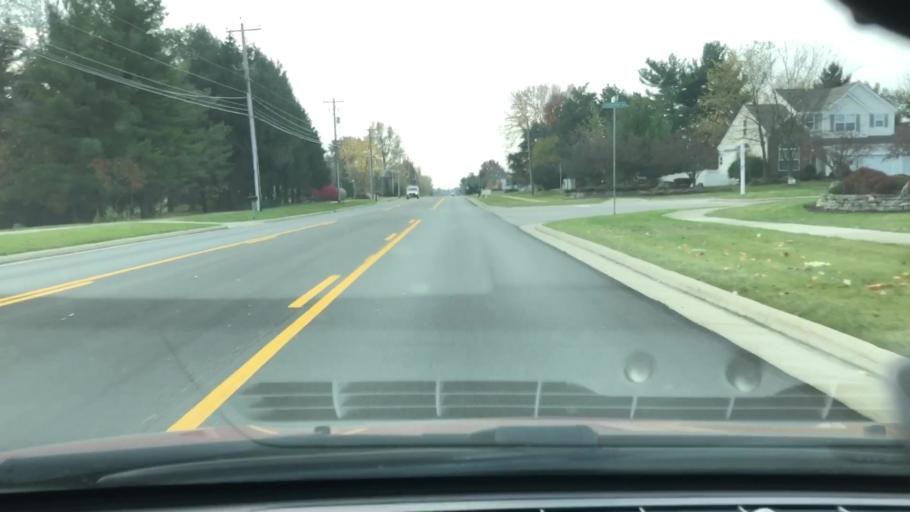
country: US
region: Ohio
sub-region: Franklin County
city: Westerville
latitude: 40.1516
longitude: -82.9011
